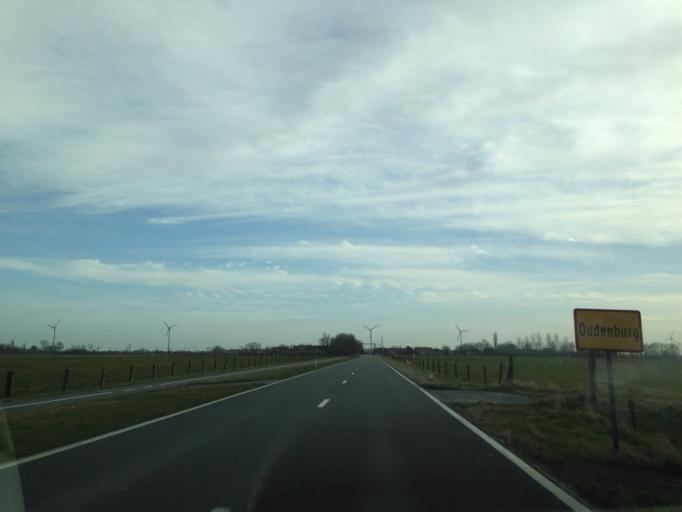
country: BE
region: Flanders
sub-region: Provincie West-Vlaanderen
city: Gistel
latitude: 51.1865
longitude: 2.9618
